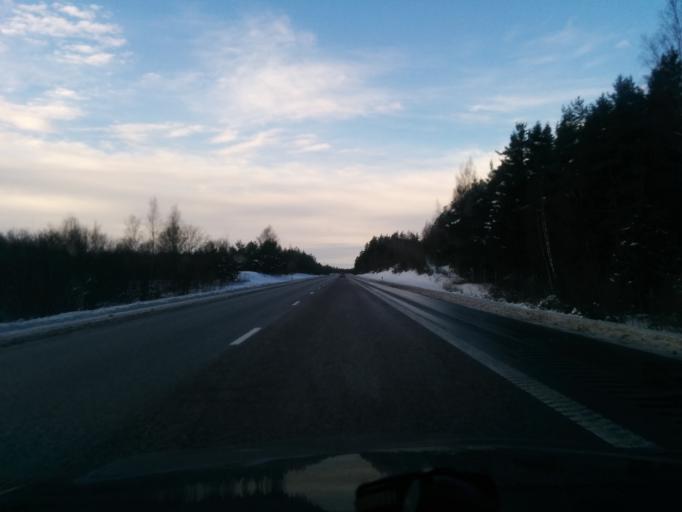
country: SE
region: Uppsala
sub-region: Enkopings Kommun
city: Dalby
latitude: 59.6078
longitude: 17.4248
